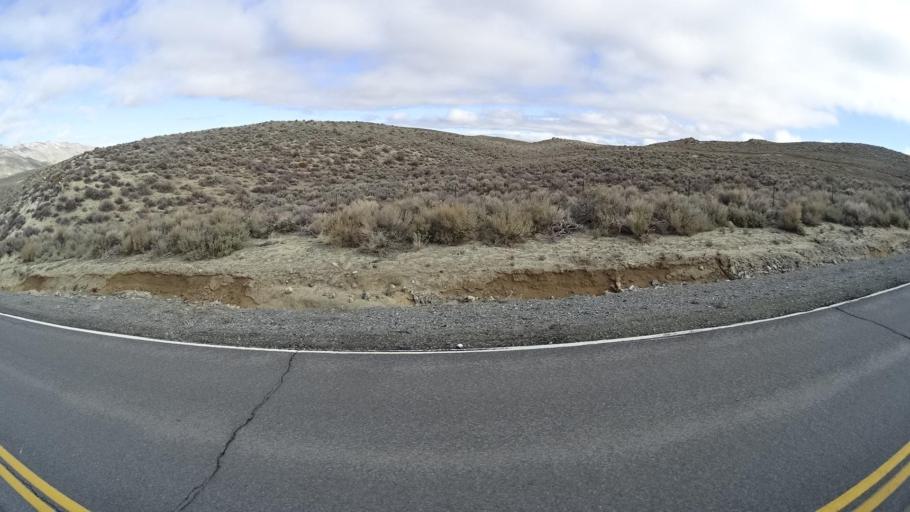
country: US
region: Nevada
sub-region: Washoe County
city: Cold Springs
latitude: 39.8031
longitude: -119.9147
